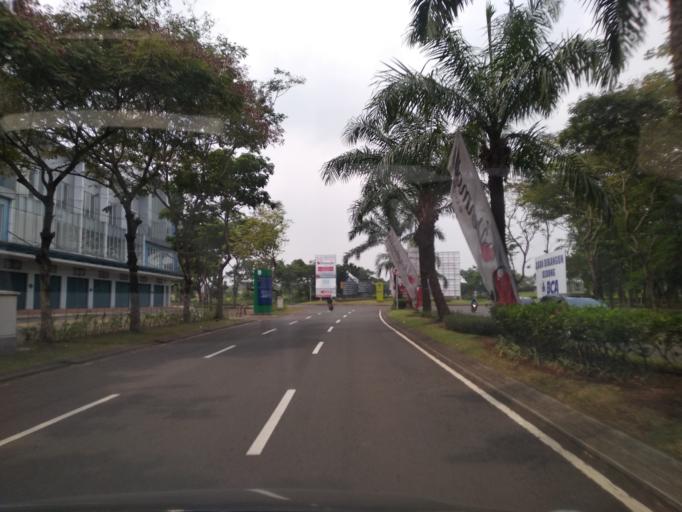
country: ID
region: West Java
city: Bekasi
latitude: -6.2913
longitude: 107.0451
